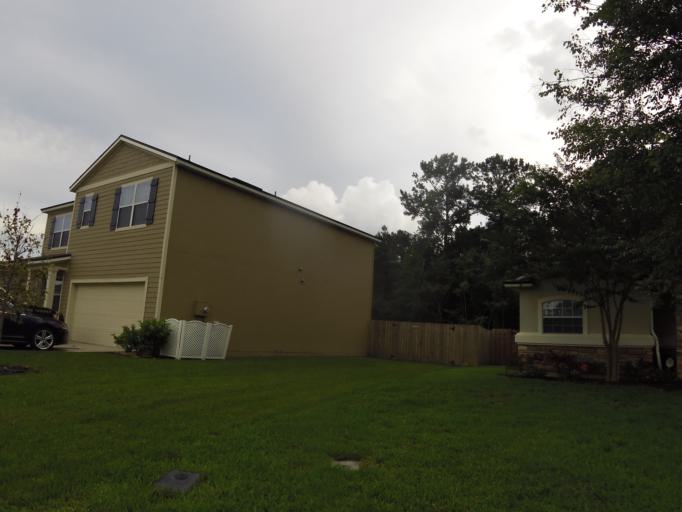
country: US
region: Florida
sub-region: Nassau County
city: Callahan
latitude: 30.5717
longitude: -81.8323
